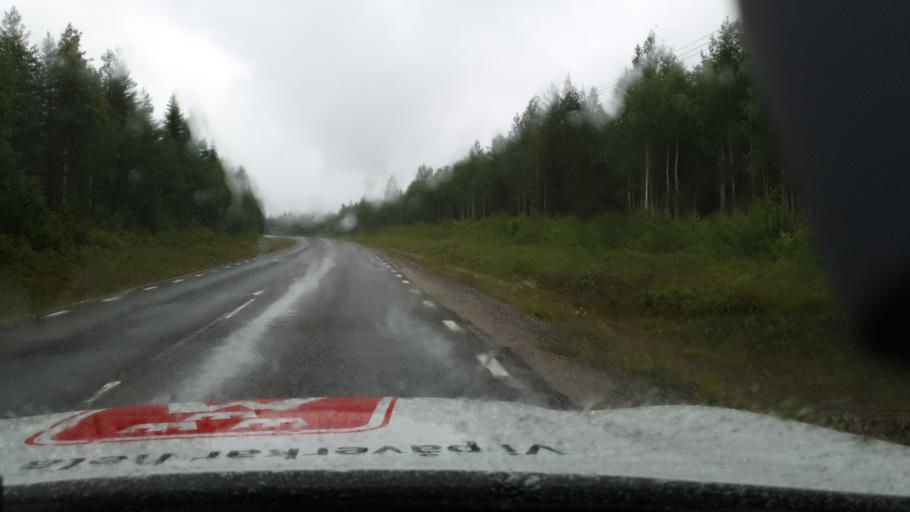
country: SE
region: Vaesterbotten
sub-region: Lycksele Kommun
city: Lycksele
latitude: 64.5374
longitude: 18.4921
